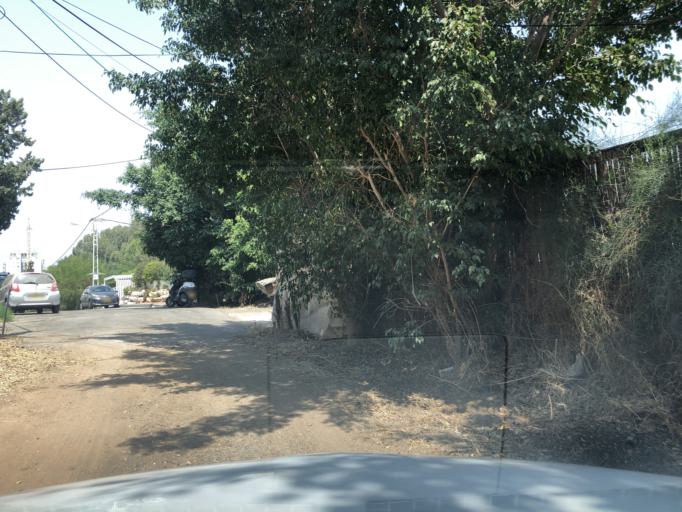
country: IL
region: Central District
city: Ganne Tiqwa
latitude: 32.0680
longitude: 34.8748
